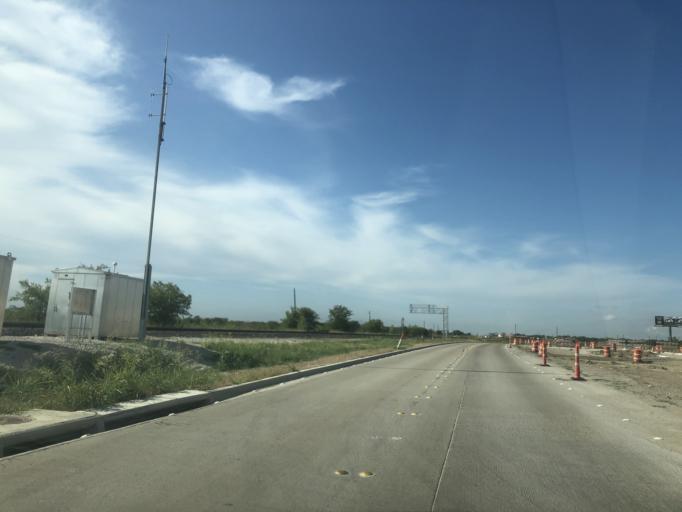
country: US
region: Texas
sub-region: Denton County
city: Justin
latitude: 33.0588
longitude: -97.2988
